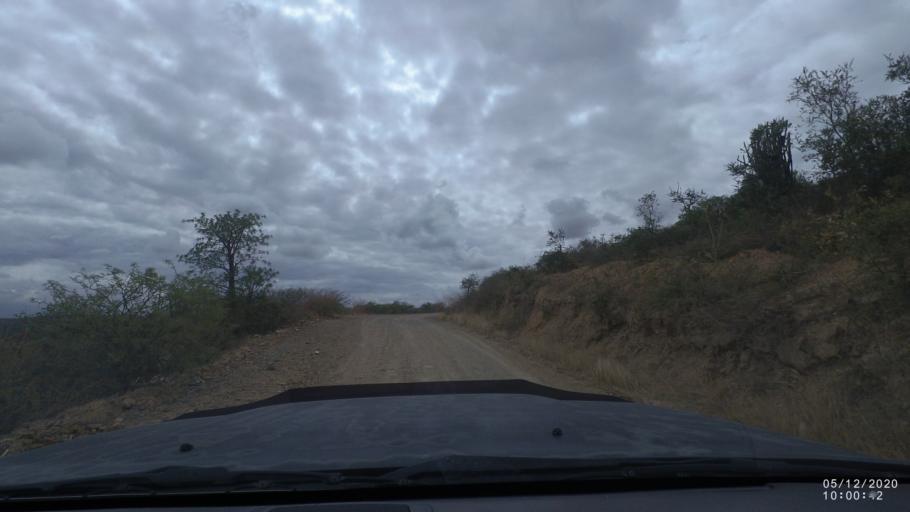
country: BO
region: Cochabamba
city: Sipe Sipe
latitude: -17.4379
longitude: -66.2862
